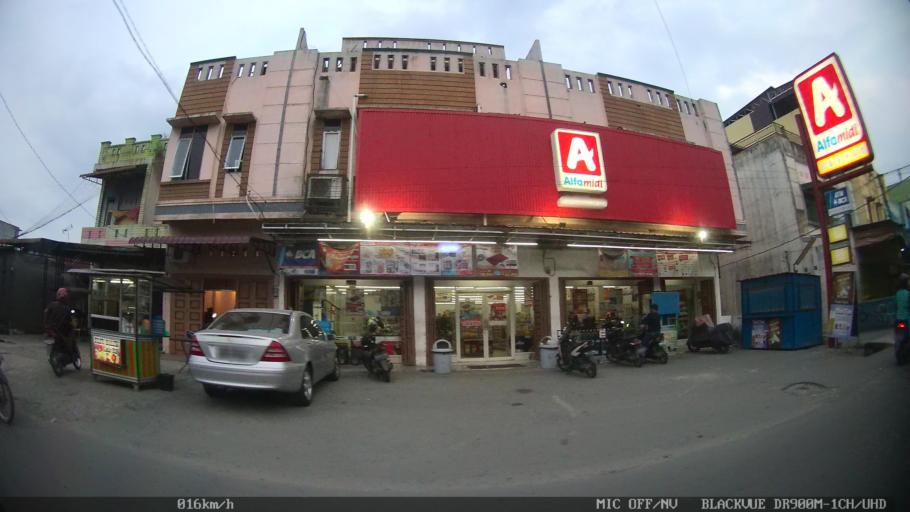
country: ID
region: North Sumatra
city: Sunggal
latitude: 3.5881
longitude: 98.6006
